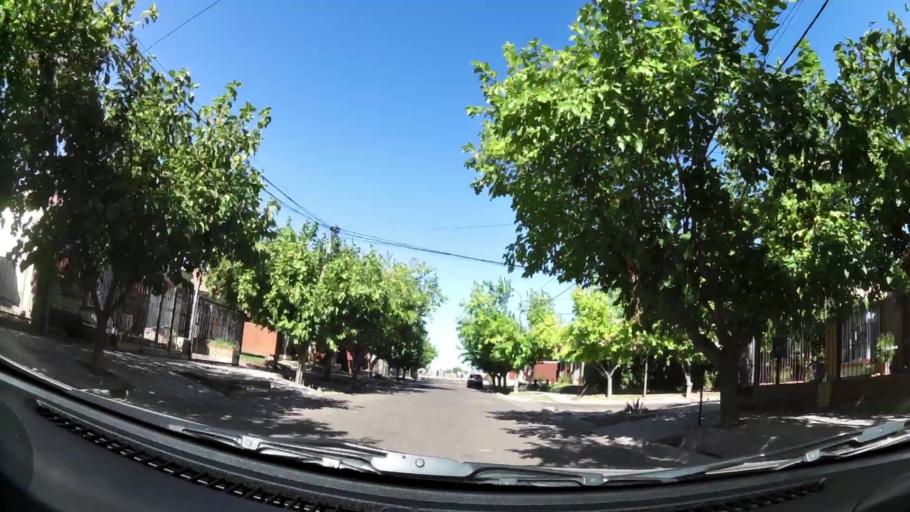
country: AR
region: Mendoza
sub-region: Departamento de Godoy Cruz
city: Godoy Cruz
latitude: -32.9422
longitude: -68.8055
